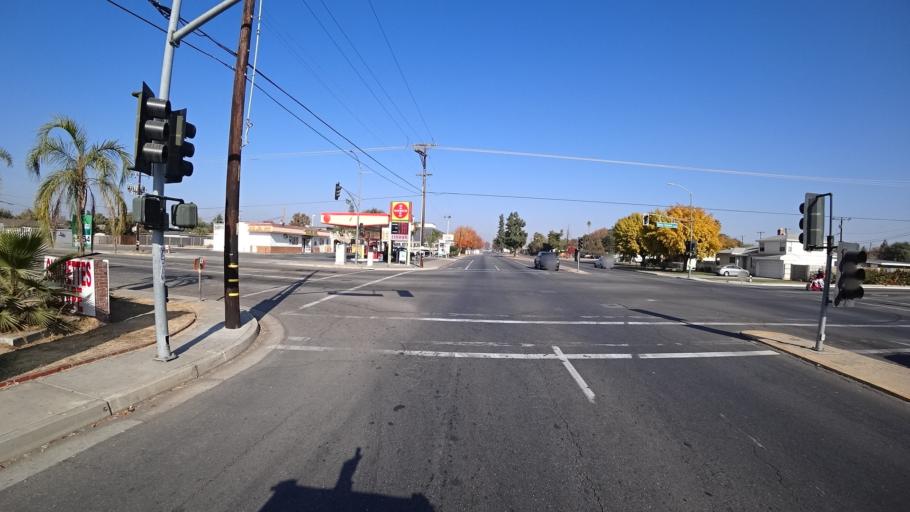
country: US
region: California
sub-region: Kern County
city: Bakersfield
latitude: 35.3465
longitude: -119.0213
